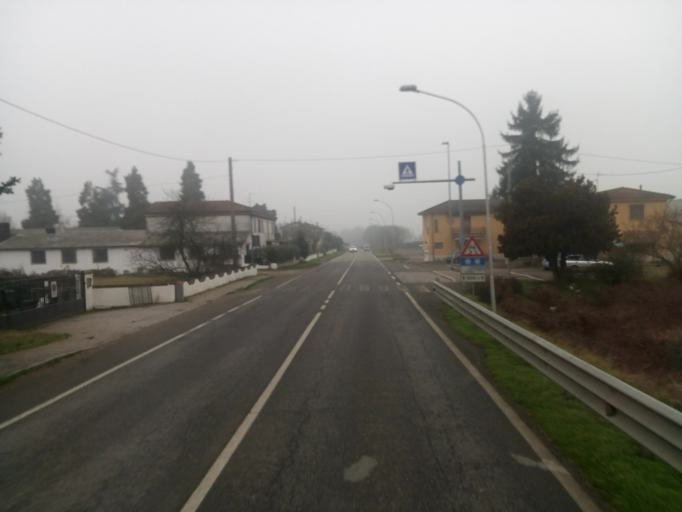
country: IT
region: Lombardy
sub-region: Provincia di Cremona
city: Sesto Cremonese
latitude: 45.1649
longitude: 9.9104
